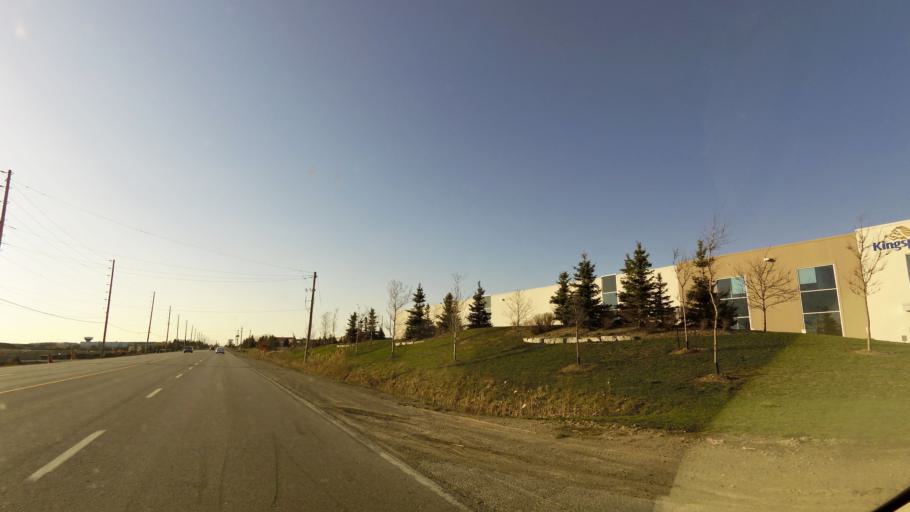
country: CA
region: Ontario
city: Brampton
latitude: 43.8497
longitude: -79.7206
